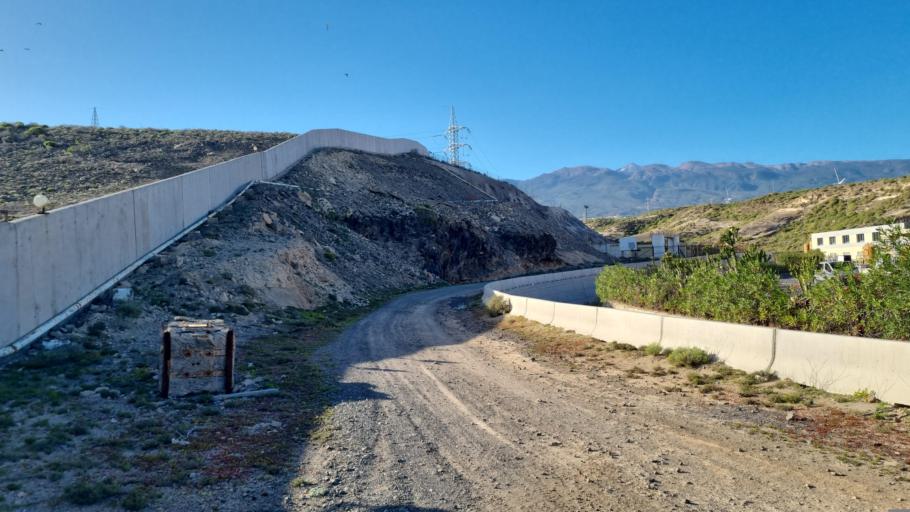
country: ES
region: Canary Islands
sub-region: Provincia de Santa Cruz de Tenerife
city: San Isidro
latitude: 28.0877
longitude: -16.4924
